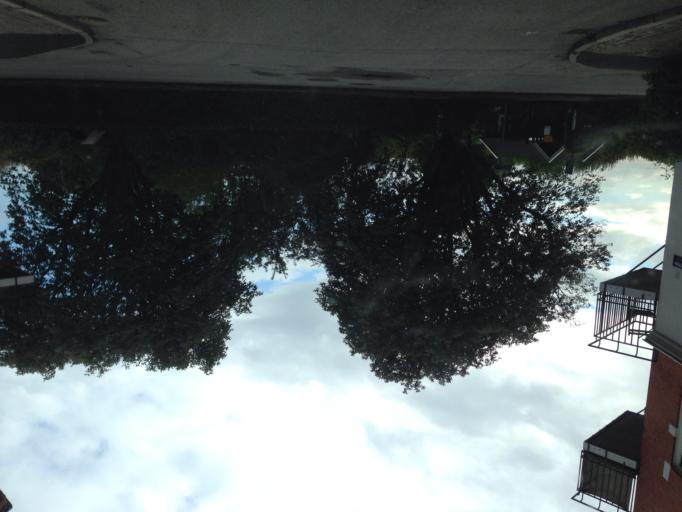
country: SE
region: Skane
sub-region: Lunds Kommun
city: Lund
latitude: 55.7015
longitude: 13.1807
